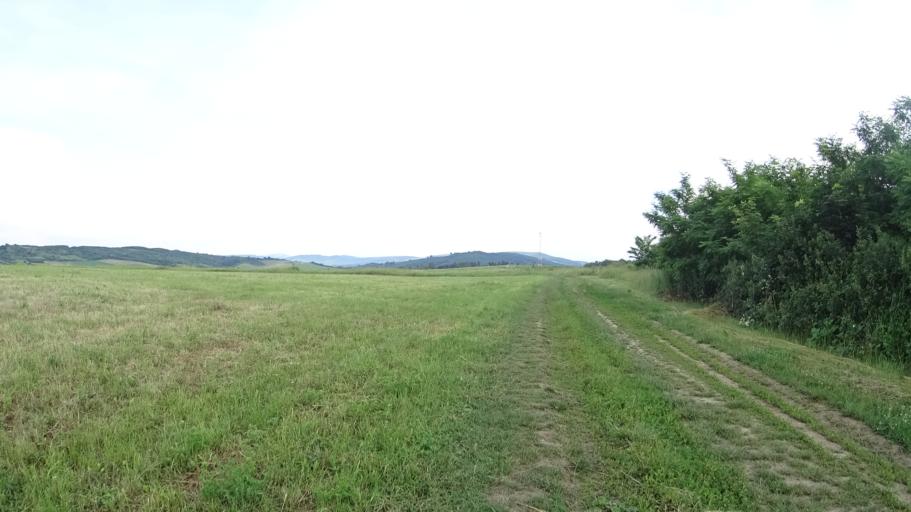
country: HU
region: Nograd
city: Retsag
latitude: 47.9263
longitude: 19.1558
